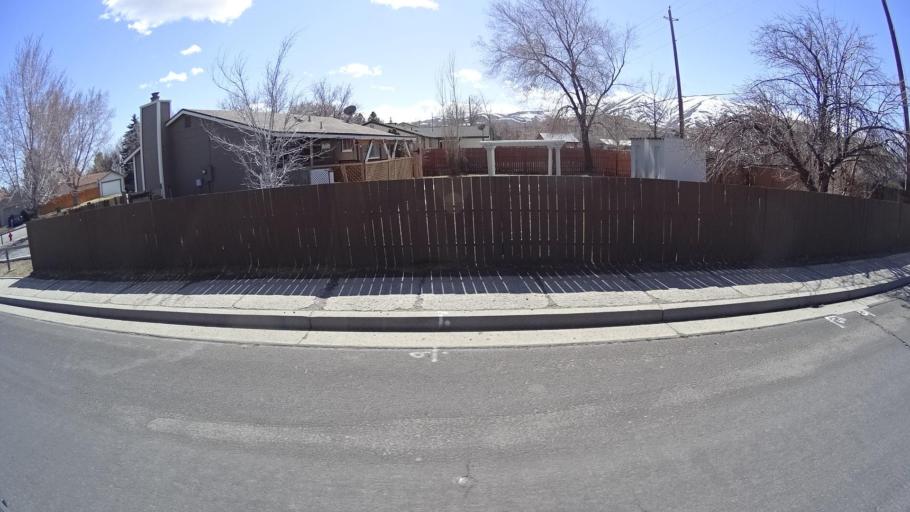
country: US
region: Nevada
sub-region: Washoe County
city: Lemmon Valley
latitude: 39.6423
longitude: -119.8789
